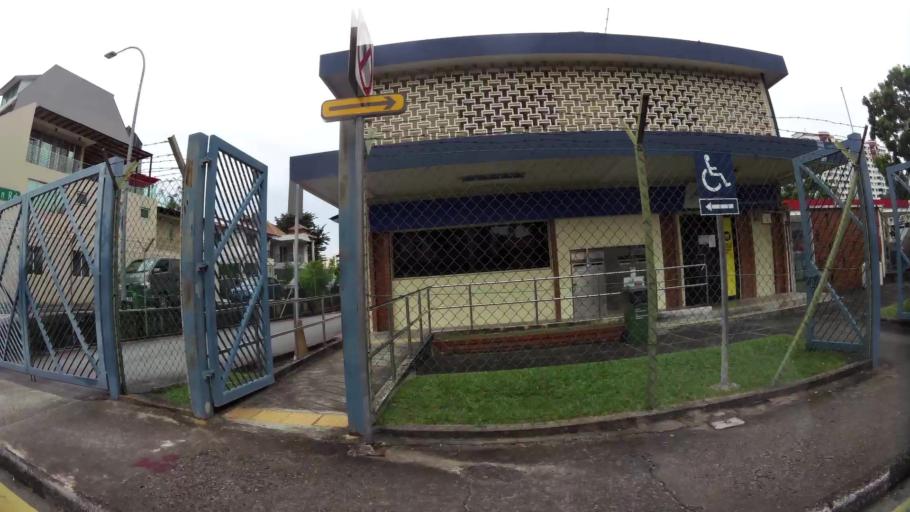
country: SG
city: Singapore
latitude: 1.3633
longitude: 103.8877
